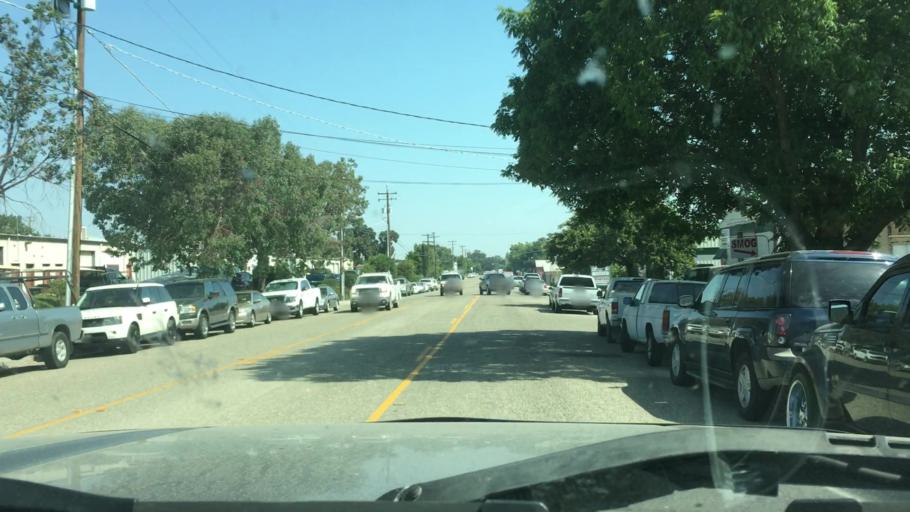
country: US
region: California
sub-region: San Luis Obispo County
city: Paso Robles
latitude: 35.6231
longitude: -120.6853
